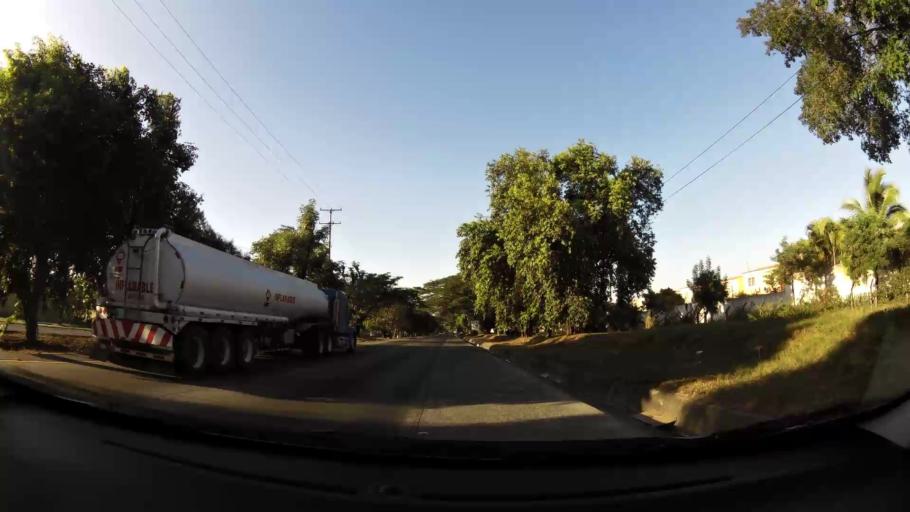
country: SV
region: La Libertad
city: Santa Tecla
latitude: 13.7457
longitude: -89.3637
